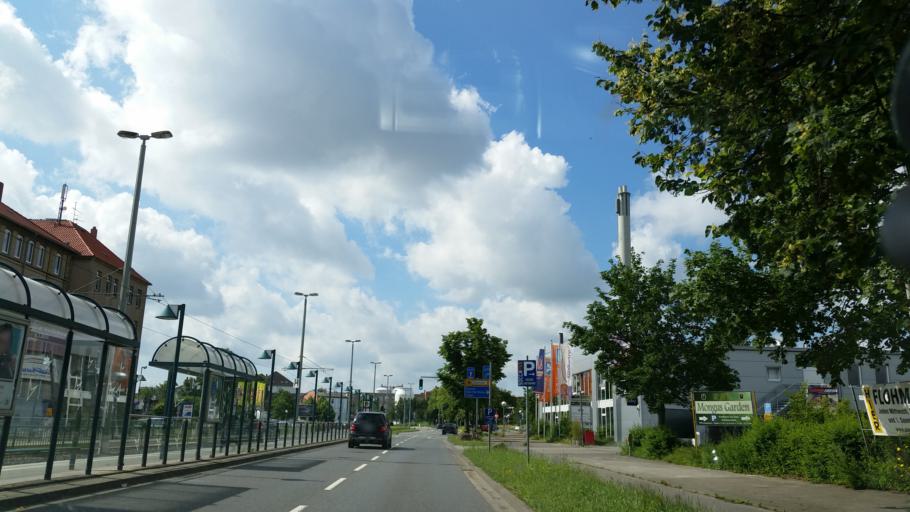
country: DE
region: Lower Saxony
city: Braunschweig
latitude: 52.2837
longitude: 10.5187
